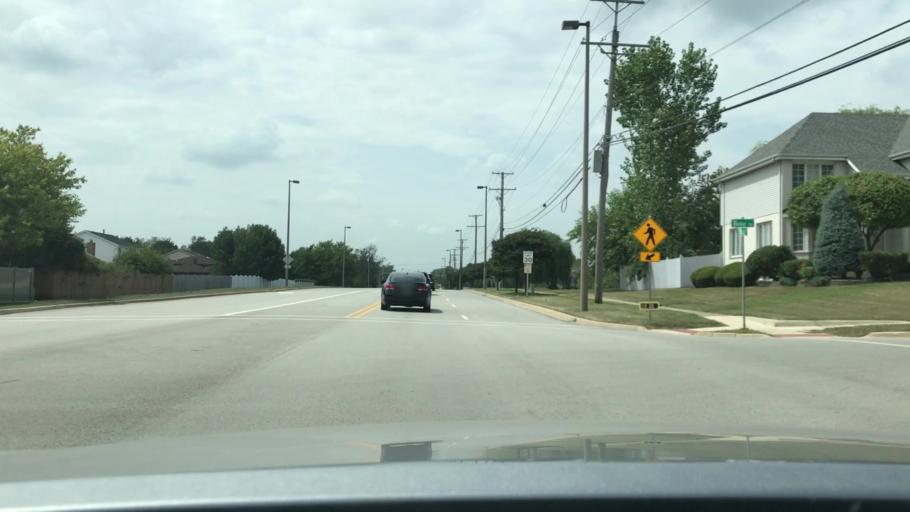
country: US
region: Illinois
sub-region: DuPage County
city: Woodridge
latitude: 41.7363
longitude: -88.0262
